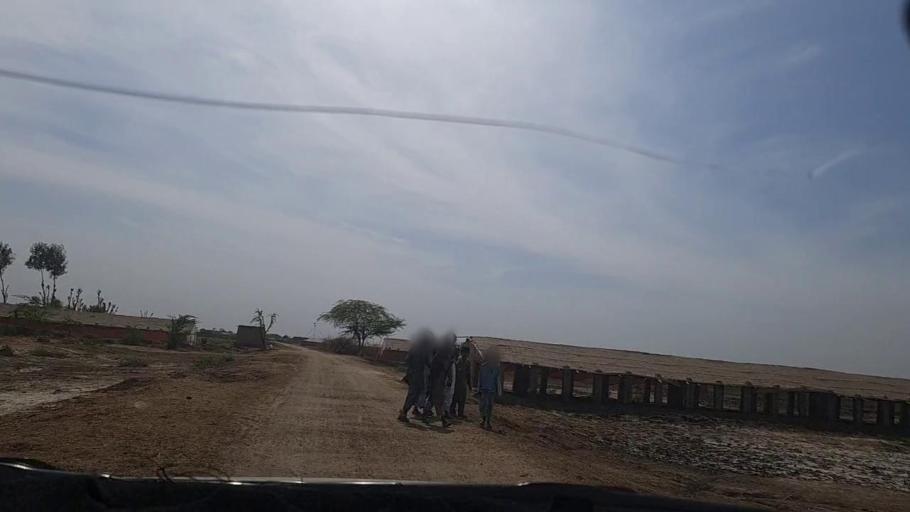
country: PK
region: Sindh
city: Dhoro Naro
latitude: 25.4395
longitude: 69.4975
